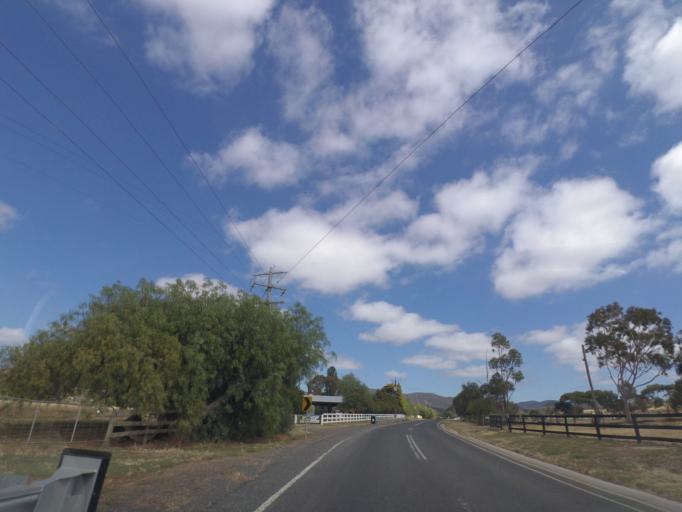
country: AU
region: Victoria
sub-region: Moorabool
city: Bacchus Marsh
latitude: -37.6445
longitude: 144.4429
